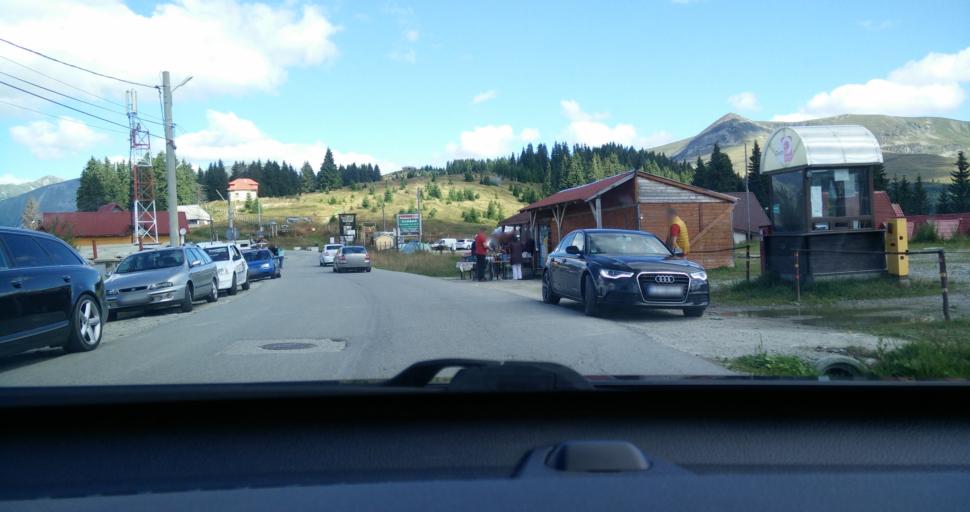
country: RO
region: Gorj
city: Novaci-Straini
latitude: 45.2916
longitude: 23.6889
